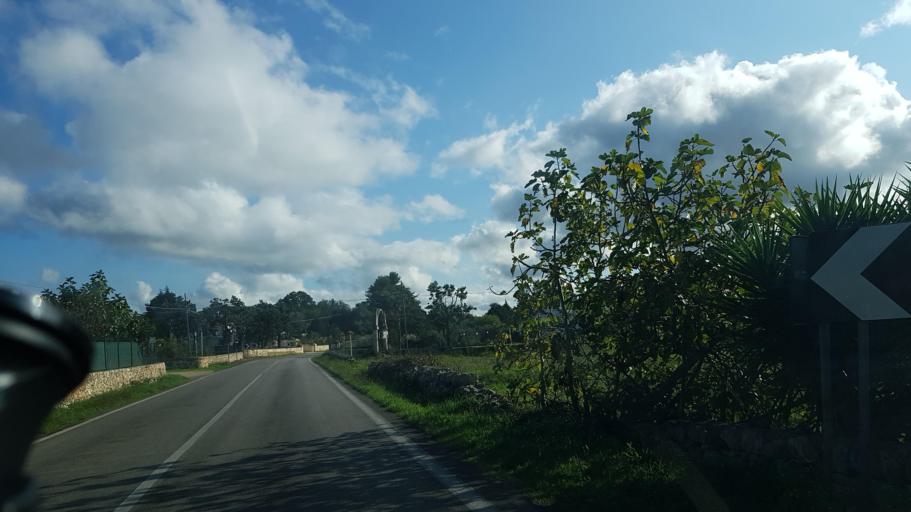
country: IT
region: Apulia
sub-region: Provincia di Brindisi
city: Ostuni
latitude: 40.6967
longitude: 17.5863
